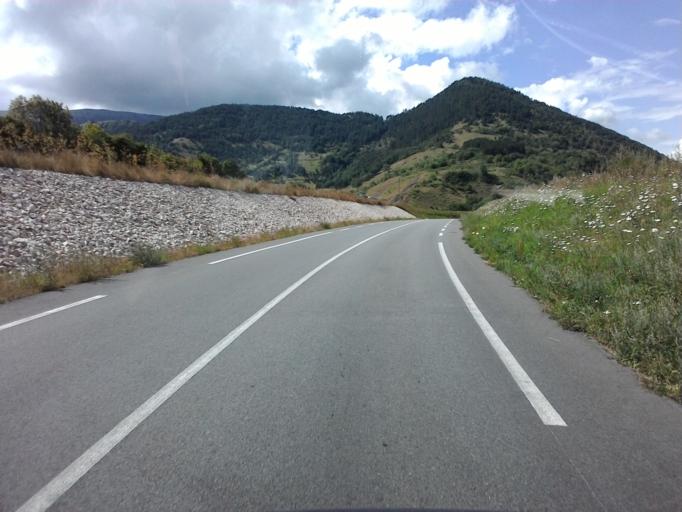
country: FR
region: Rhone-Alpes
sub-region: Departement de l'Isere
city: La Mure
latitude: 44.8972
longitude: 5.7826
